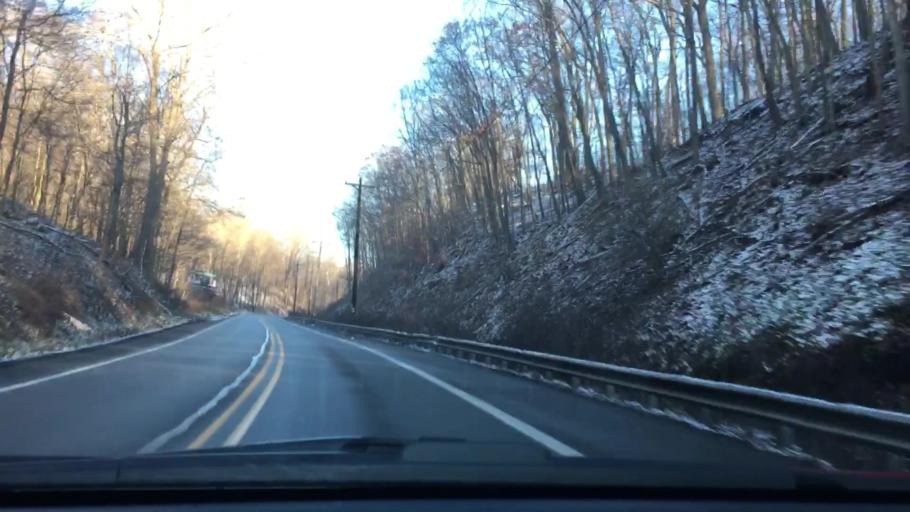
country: US
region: Pennsylvania
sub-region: Allegheny County
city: Glassport
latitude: 40.3303
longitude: -79.9100
